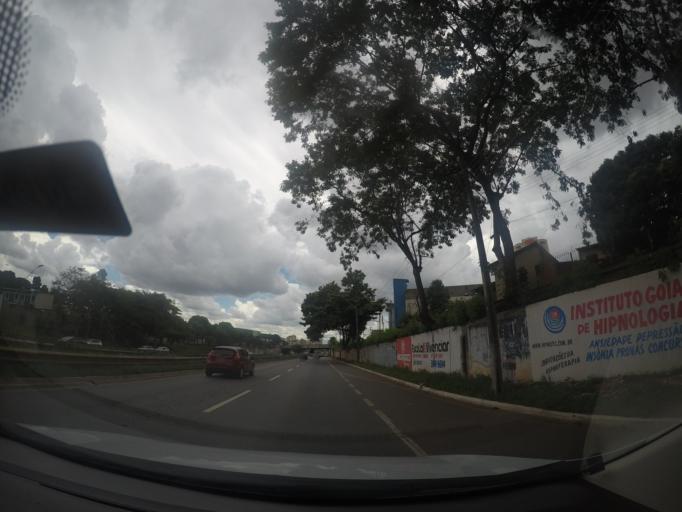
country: BR
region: Goias
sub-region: Goiania
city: Goiania
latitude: -16.6878
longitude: -49.2442
